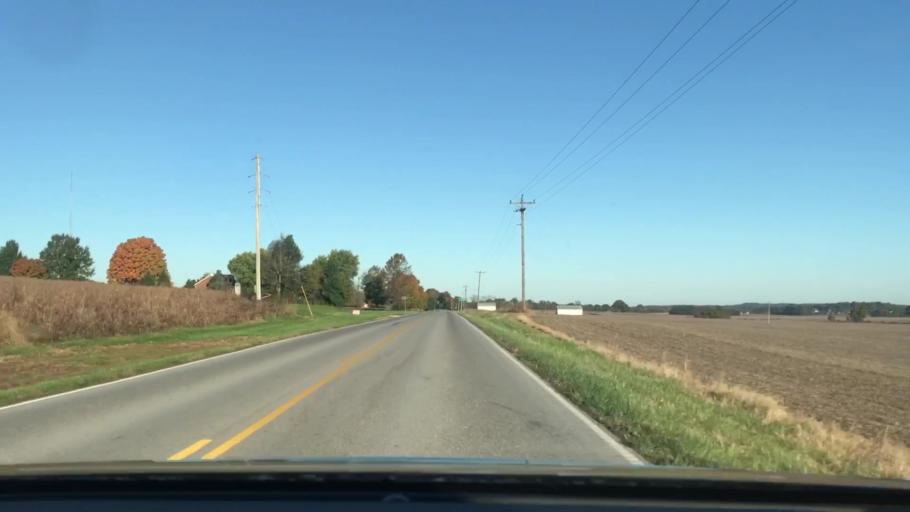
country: US
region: Kentucky
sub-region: Logan County
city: Auburn
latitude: 36.8389
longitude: -86.6912
